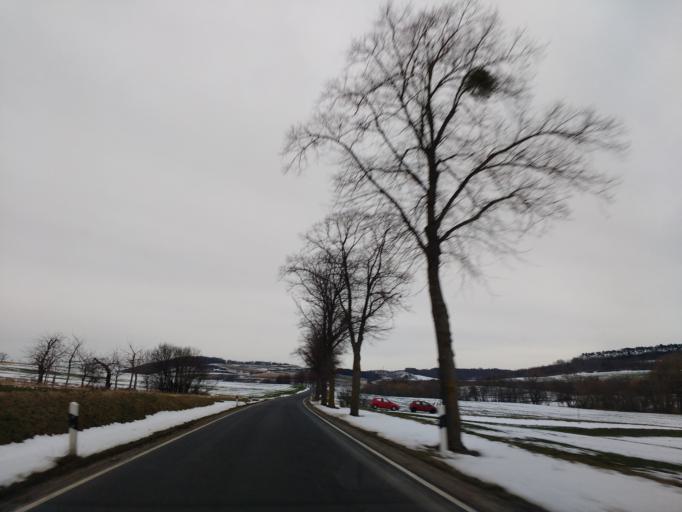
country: DE
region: Lower Saxony
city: Gemeinde Friedland
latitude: 51.3988
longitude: 9.9479
